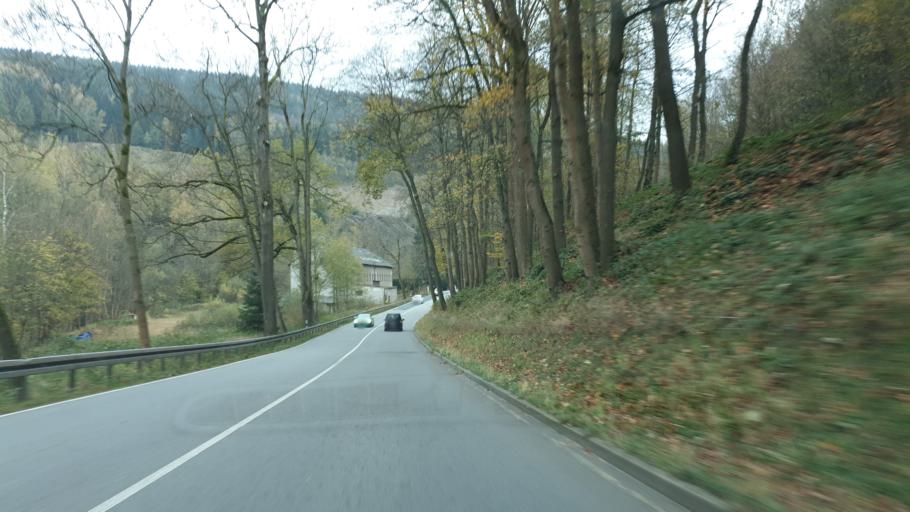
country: DE
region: Saxony
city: Schwarzenberg
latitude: 50.5078
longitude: 12.7737
